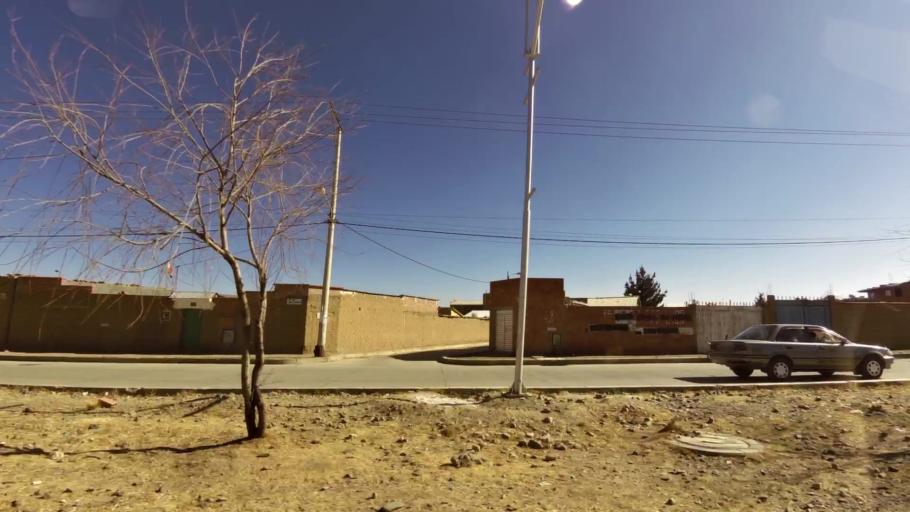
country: BO
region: La Paz
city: La Paz
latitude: -16.5301
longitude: -68.2327
